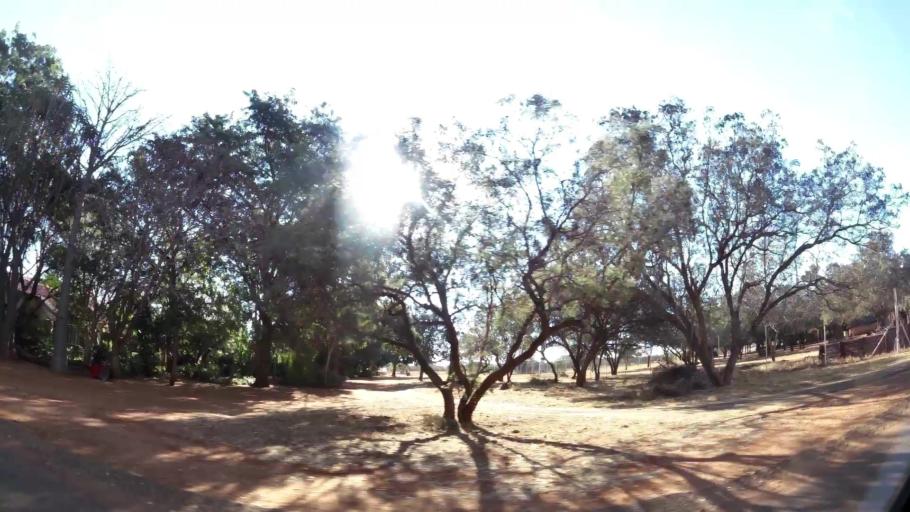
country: ZA
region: Limpopo
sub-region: Waterberg District Municipality
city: Mokopane
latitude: -24.2049
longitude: 29.0012
